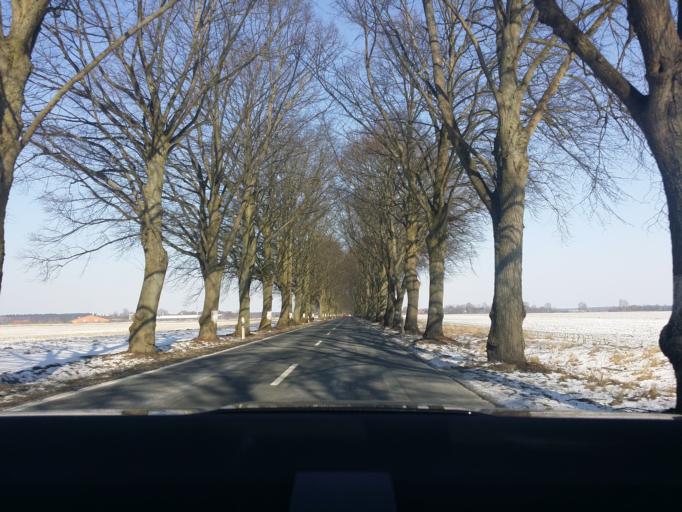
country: DE
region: Brandenburg
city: Wittstock
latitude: 53.2075
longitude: 12.5794
